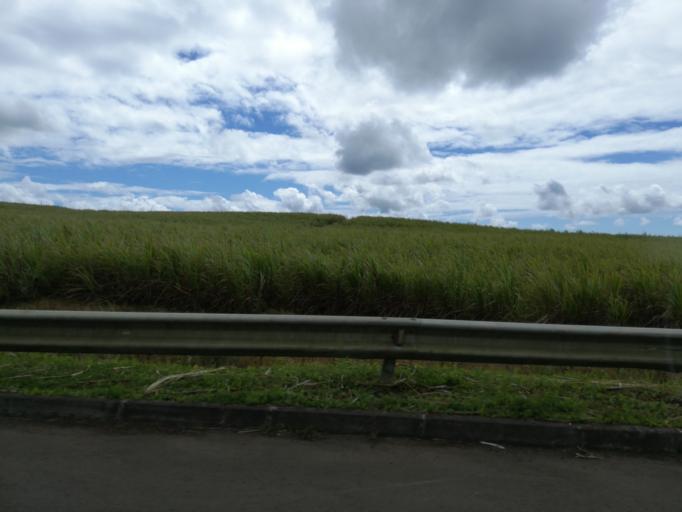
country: MU
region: Moka
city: Quartier Militaire
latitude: -20.2427
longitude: 57.5994
